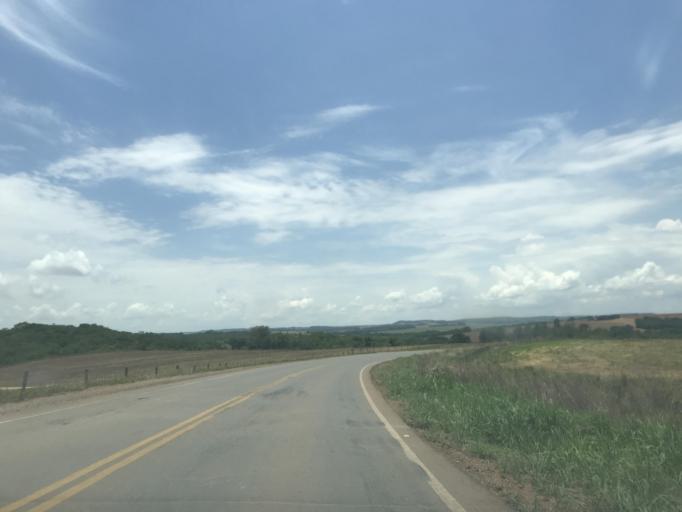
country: BR
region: Goias
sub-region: Vianopolis
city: Vianopolis
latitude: -16.6345
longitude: -48.3557
